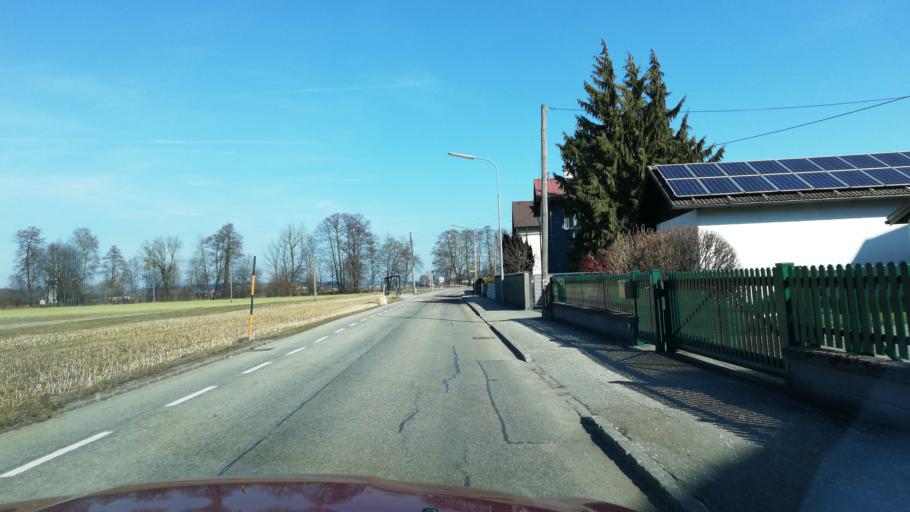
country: AT
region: Upper Austria
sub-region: Politischer Bezirk Vocklabruck
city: Redlham
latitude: 48.0209
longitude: 13.7375
